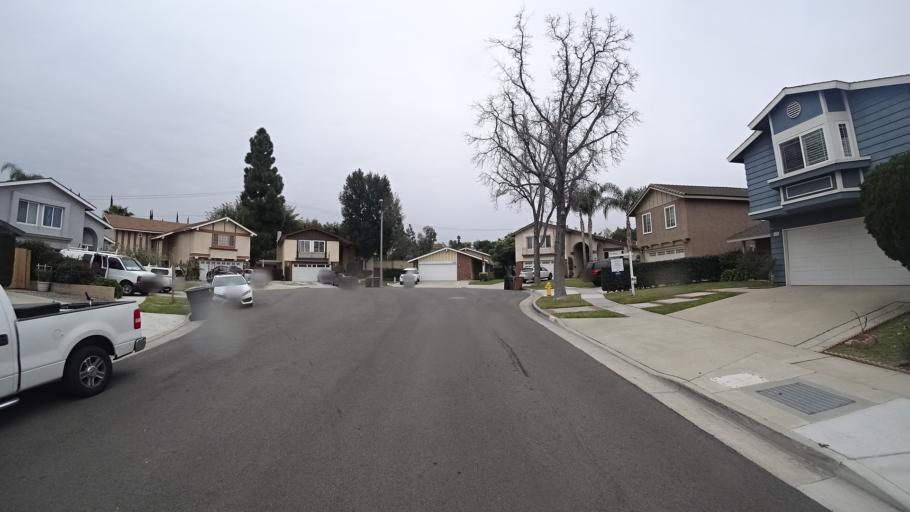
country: US
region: California
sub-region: Orange County
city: Yorba Linda
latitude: 33.8529
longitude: -117.7950
